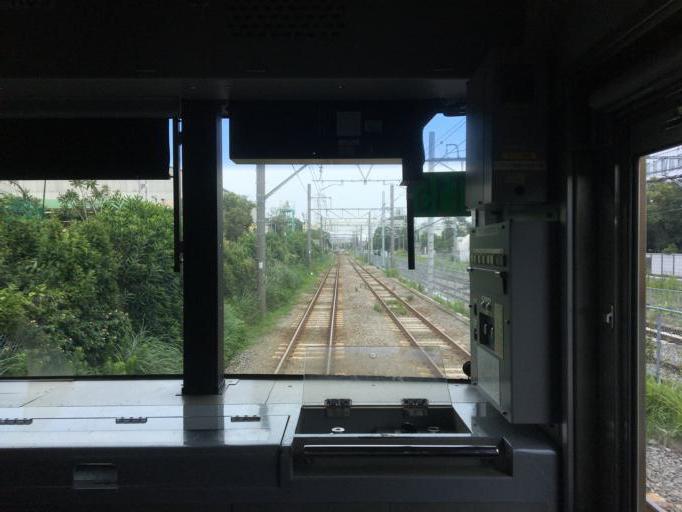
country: JP
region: Kanagawa
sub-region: Kawasaki-shi
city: Kawasaki
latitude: 35.4966
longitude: 139.6920
